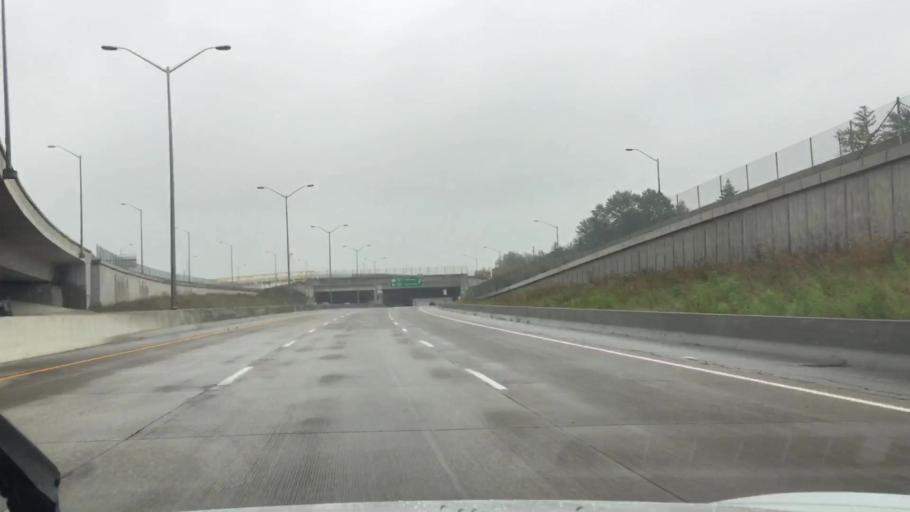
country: CA
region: Ontario
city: Windsor
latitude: 42.2378
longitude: -83.0029
